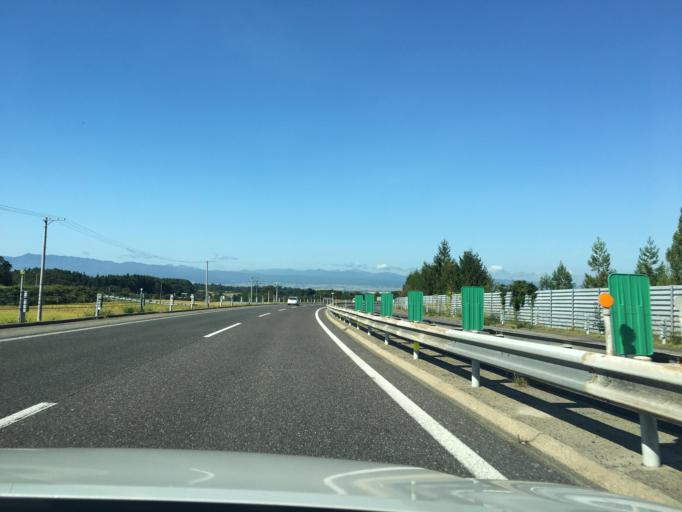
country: JP
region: Fukushima
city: Inawashiro
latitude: 37.5431
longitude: 139.9905
